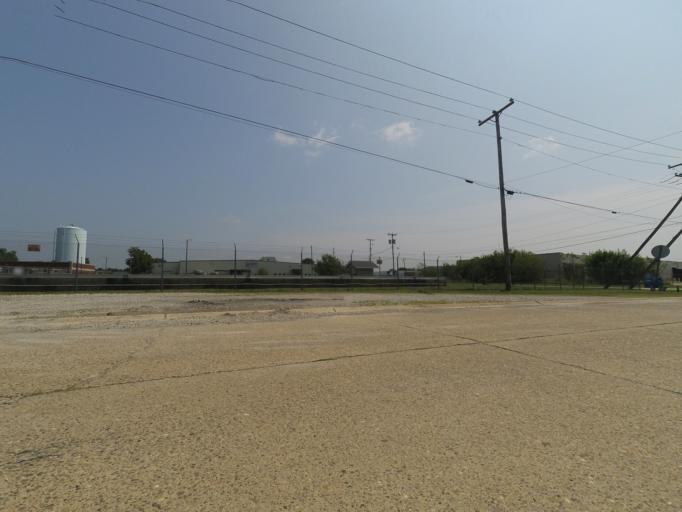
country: US
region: West Virginia
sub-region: Cabell County
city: Huntington
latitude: 38.4305
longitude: -82.4175
